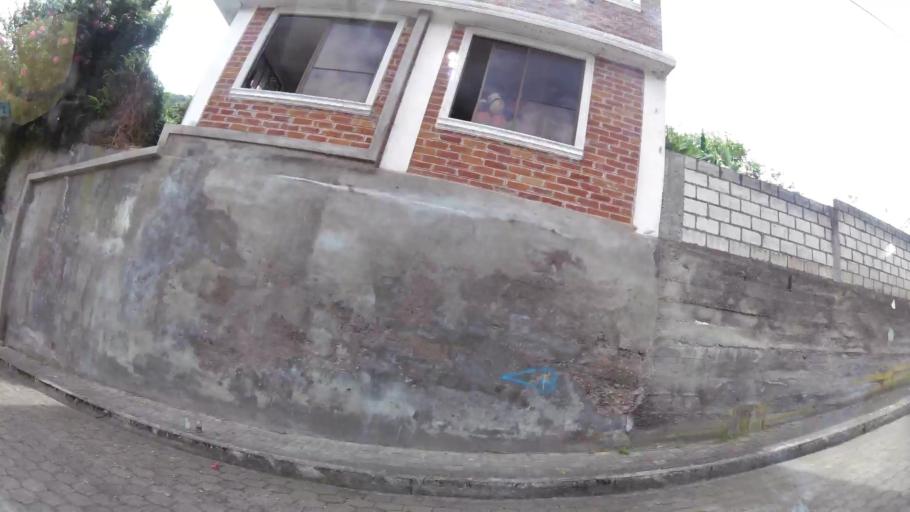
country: EC
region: Tungurahua
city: Banos
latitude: -1.3987
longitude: -78.4273
